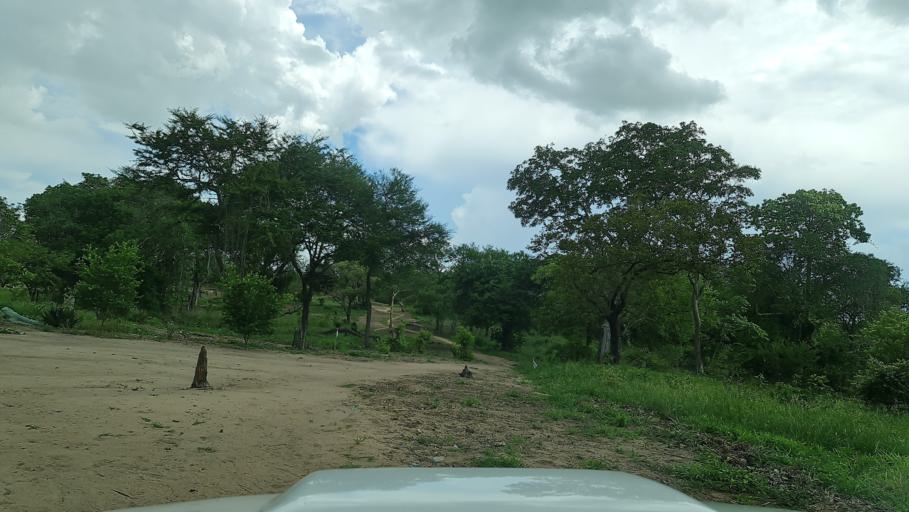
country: MZ
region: Nampula
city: Ilha de Mocambique
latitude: -15.5002
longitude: 40.1588
